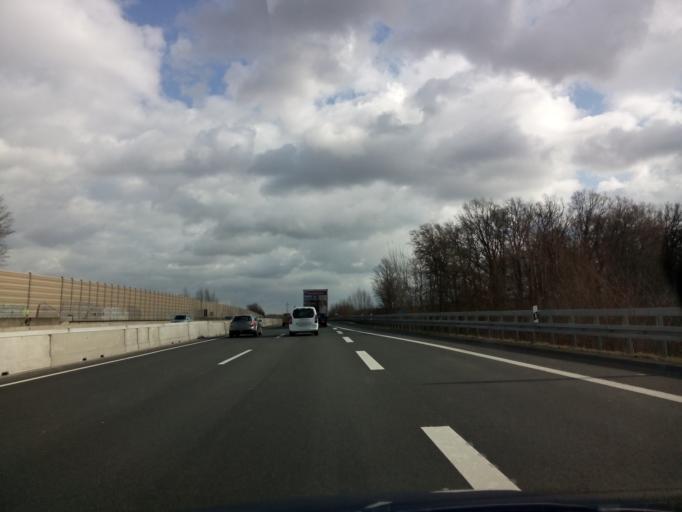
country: DE
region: Lower Saxony
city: Osnabrueck
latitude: 52.2434
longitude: 8.0985
